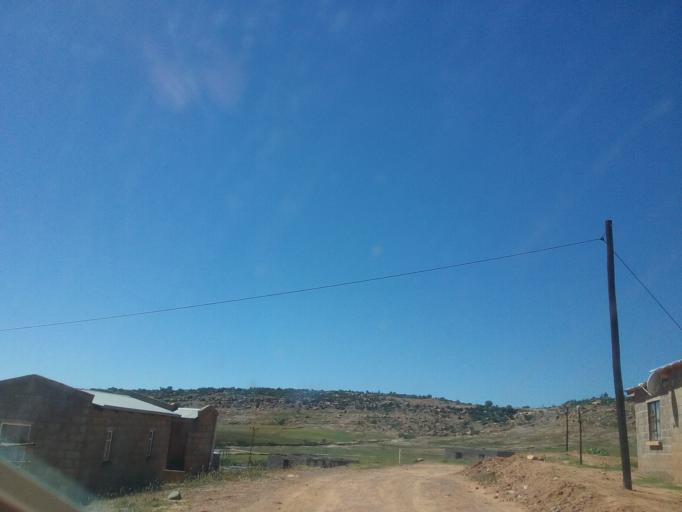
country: LS
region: Maseru
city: Maseru
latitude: -29.4019
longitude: 27.5735
